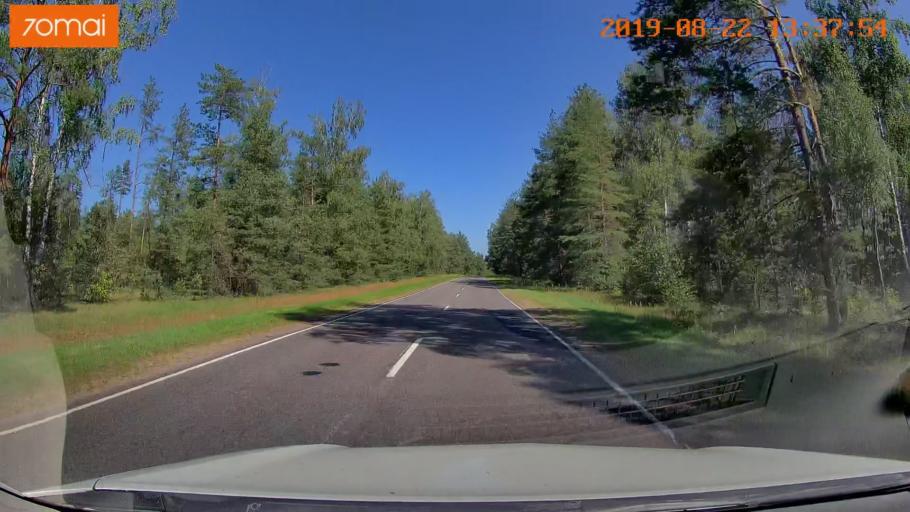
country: BY
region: Minsk
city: Staryya Darohi
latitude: 53.2189
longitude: 28.3090
